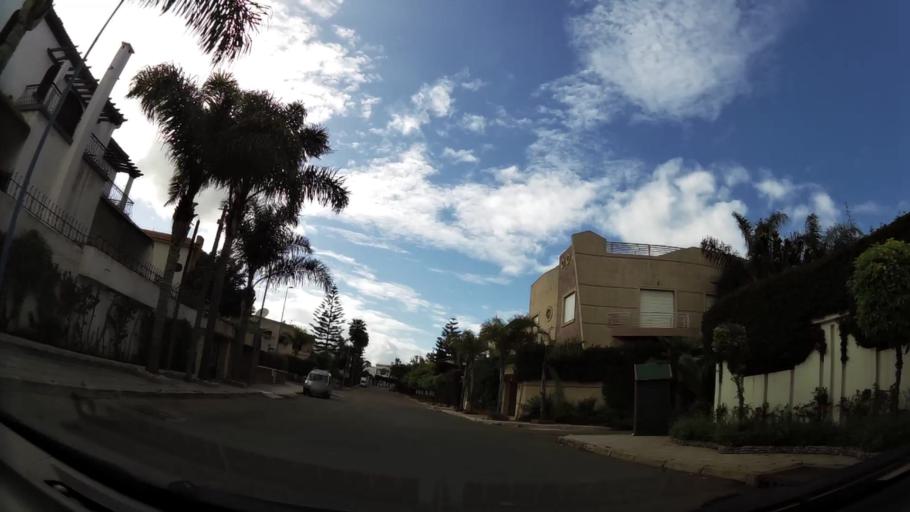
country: MA
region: Grand Casablanca
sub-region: Casablanca
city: Casablanca
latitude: 33.5457
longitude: -7.6180
